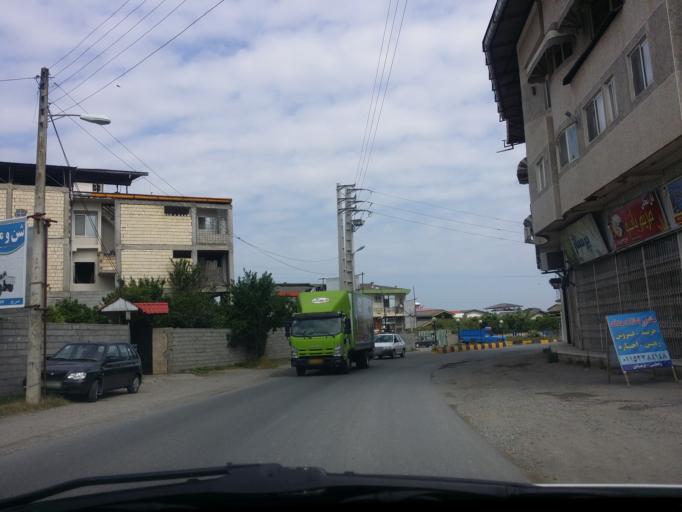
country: IR
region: Mazandaran
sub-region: Nowshahr
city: Nowshahr
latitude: 36.6280
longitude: 51.4846
